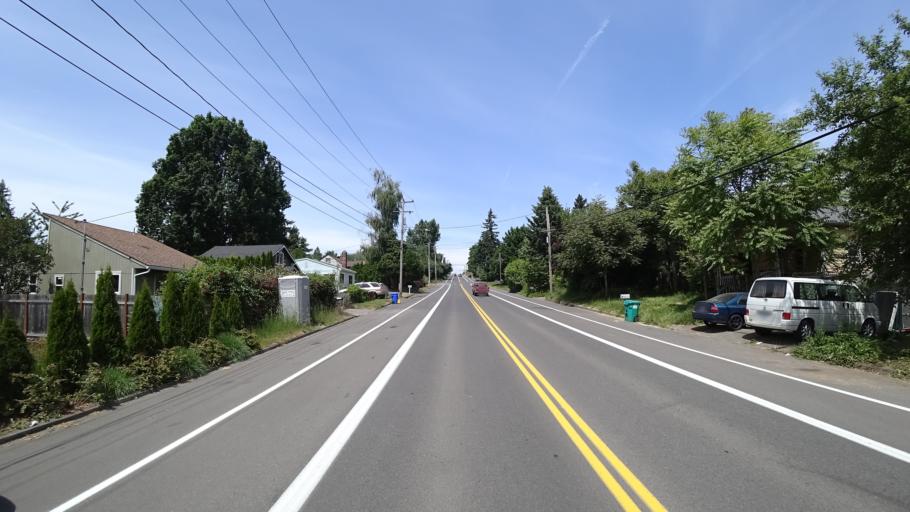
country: US
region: Oregon
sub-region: Clackamas County
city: Milwaukie
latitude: 45.4645
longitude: -122.6101
